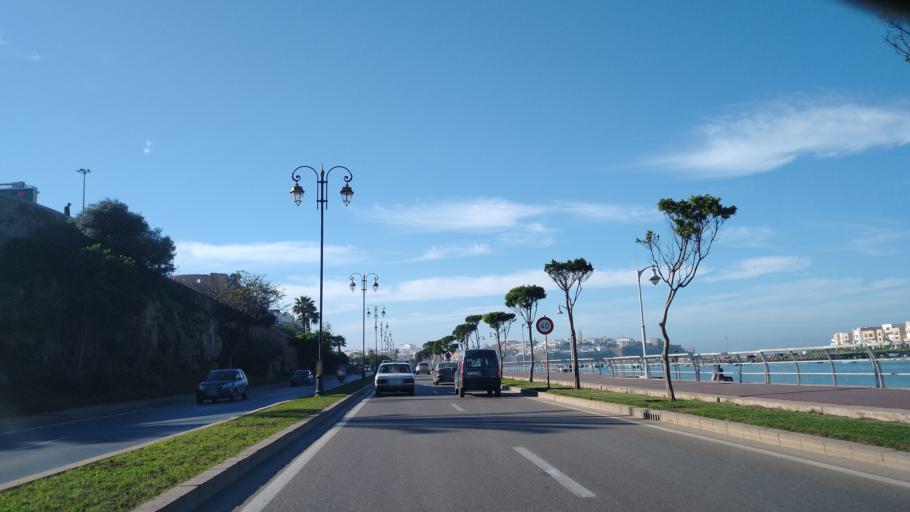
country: MA
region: Rabat-Sale-Zemmour-Zaer
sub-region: Rabat
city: Rabat
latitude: 34.0266
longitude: -6.8246
